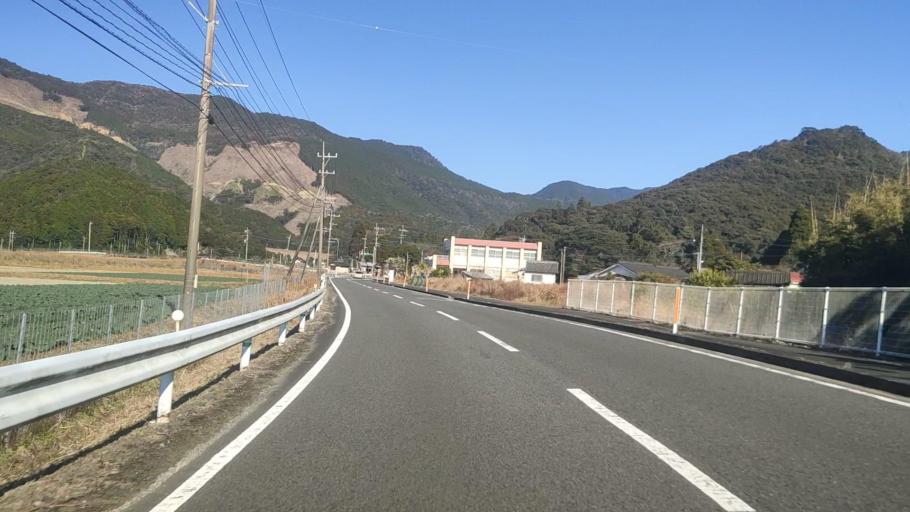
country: JP
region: Miyazaki
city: Nobeoka
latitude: 32.6824
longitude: 131.7875
